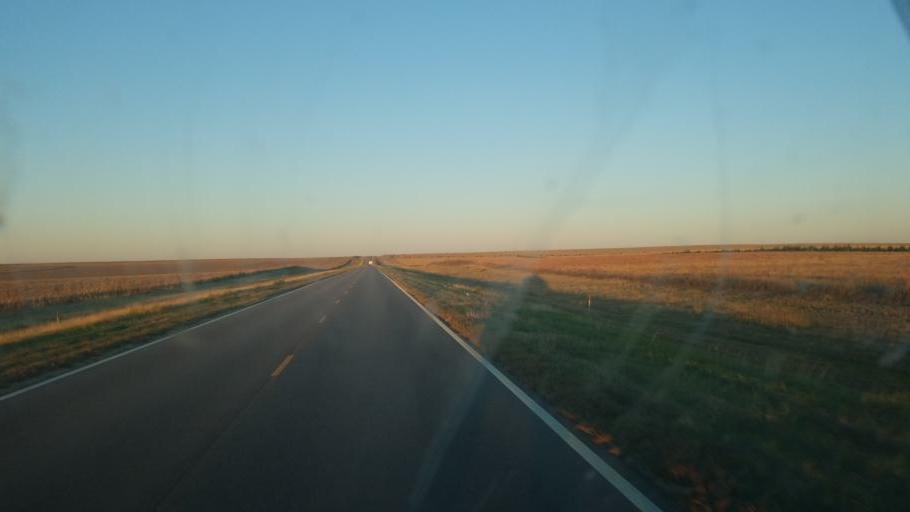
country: US
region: Kansas
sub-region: Wallace County
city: Sharon Springs
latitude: 38.9012
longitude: -101.8030
